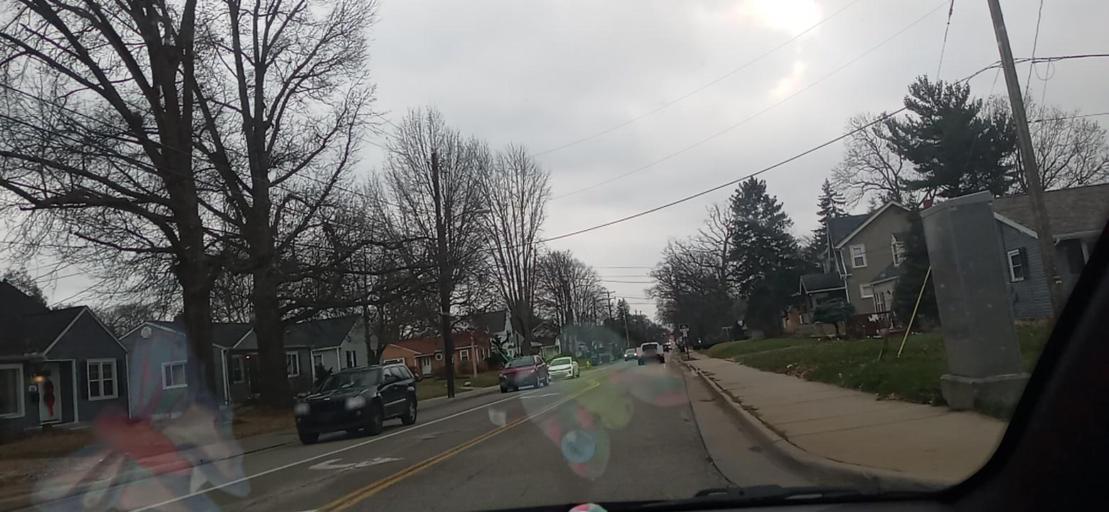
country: US
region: Ohio
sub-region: Summit County
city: Fairlawn
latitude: 41.1193
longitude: -81.5692
